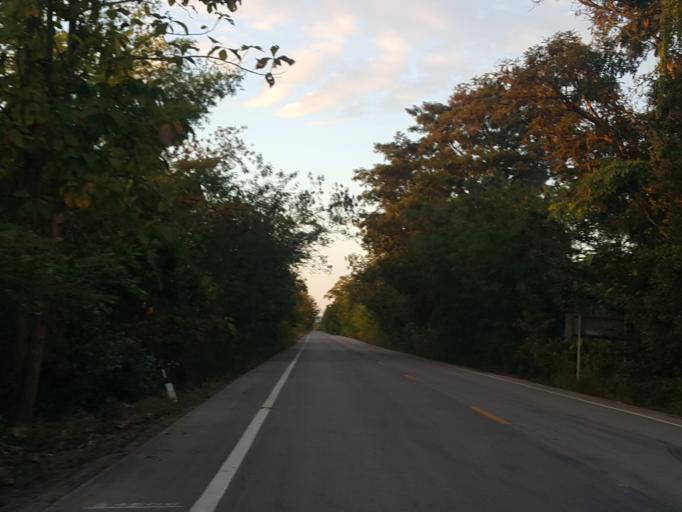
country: TH
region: Lampang
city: Mae Mo
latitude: 18.4367
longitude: 99.6403
